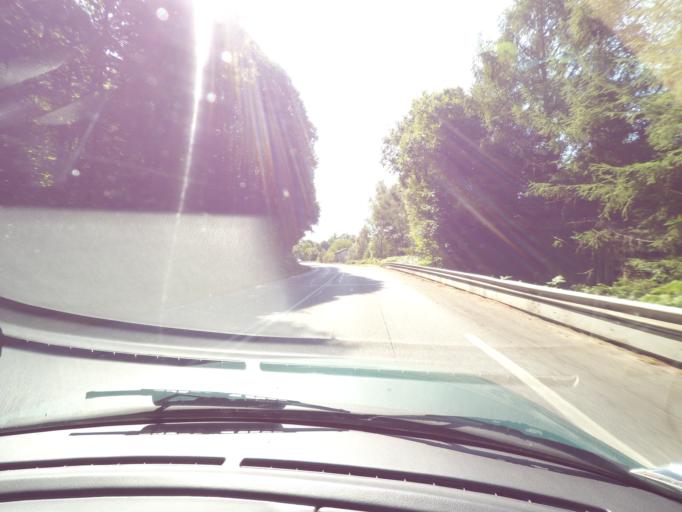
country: FR
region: Limousin
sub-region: Departement de la Haute-Vienne
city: Nieul
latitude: 45.9243
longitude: 1.1979
